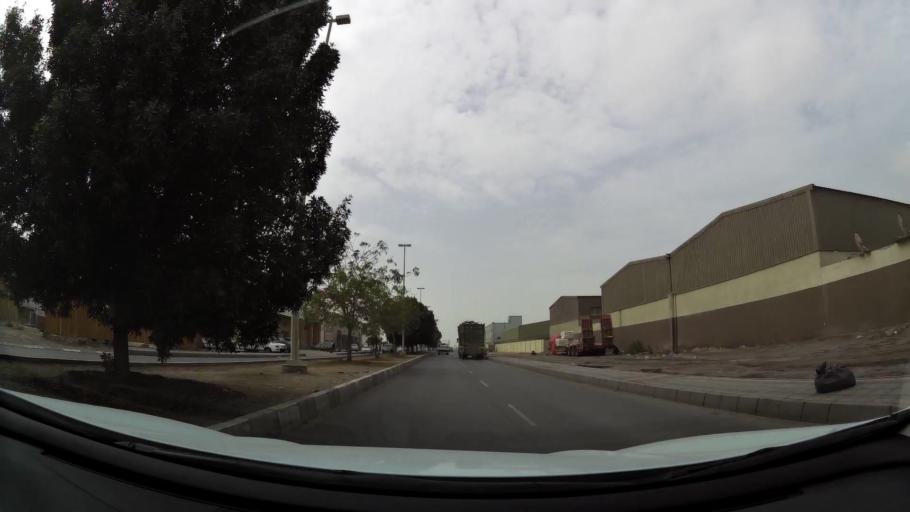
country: AE
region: Abu Dhabi
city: Abu Dhabi
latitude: 24.3543
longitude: 54.4883
